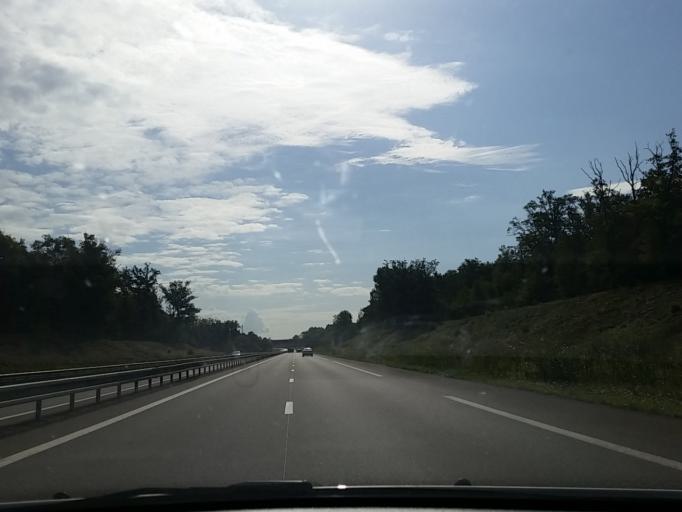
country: FR
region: Centre
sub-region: Departement du Loir-et-Cher
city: Chatres-sur-Cher
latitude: 47.2924
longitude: 1.9528
